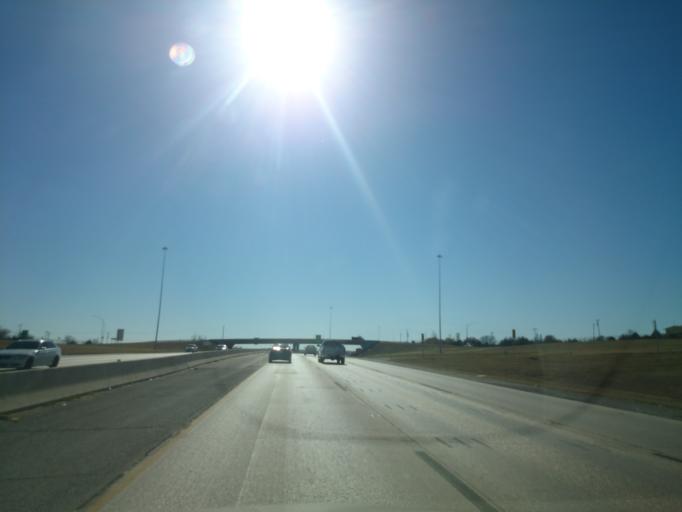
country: US
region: Oklahoma
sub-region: Oklahoma County
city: Edmond
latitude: 35.6120
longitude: -97.4250
